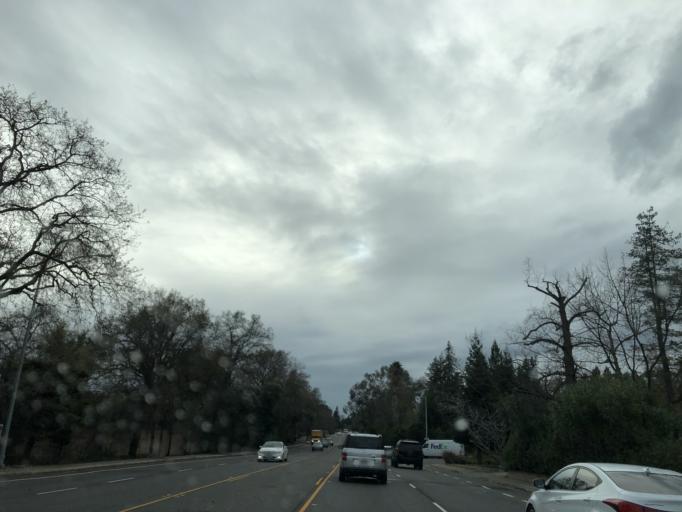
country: US
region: California
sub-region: Sacramento County
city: La Riviera
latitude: 38.5924
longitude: -121.3487
